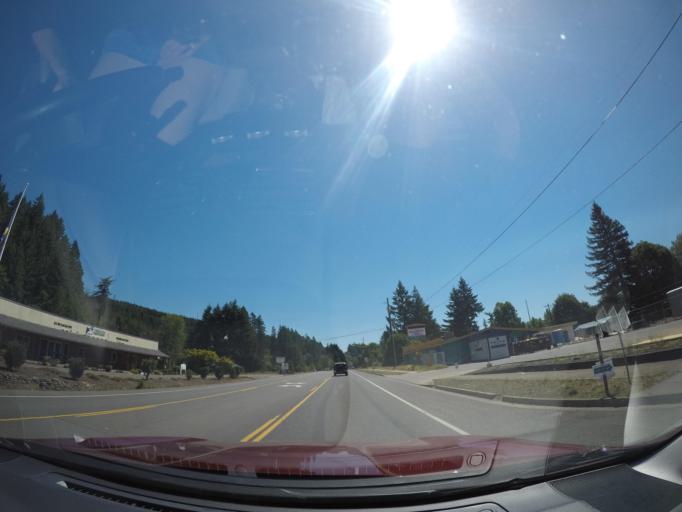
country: US
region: Oregon
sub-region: Linn County
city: Mill City
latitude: 44.7573
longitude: -122.4876
